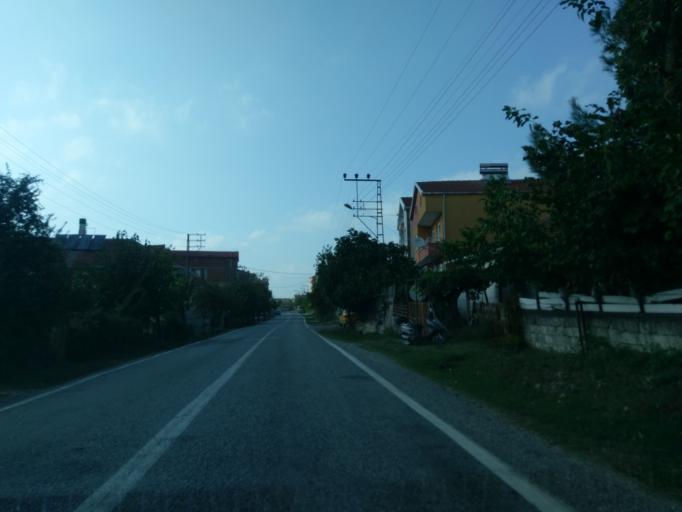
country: TR
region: Sinop
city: Helaldi
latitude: 41.9384
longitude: 34.4040
